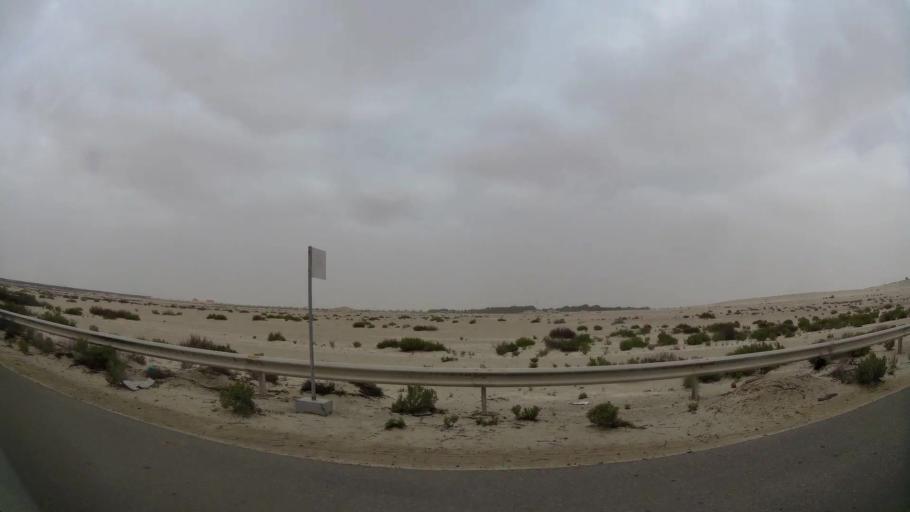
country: AE
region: Abu Dhabi
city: Abu Dhabi
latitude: 24.3988
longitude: 54.6988
